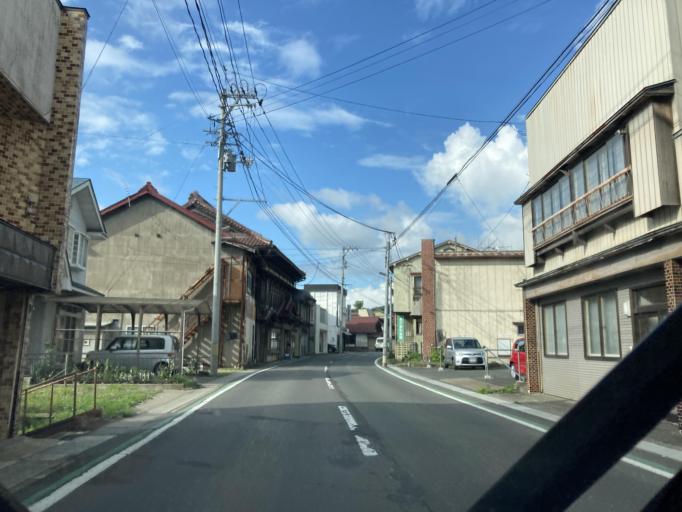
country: JP
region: Iwate
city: Ichinohe
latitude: 39.9694
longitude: 141.2218
